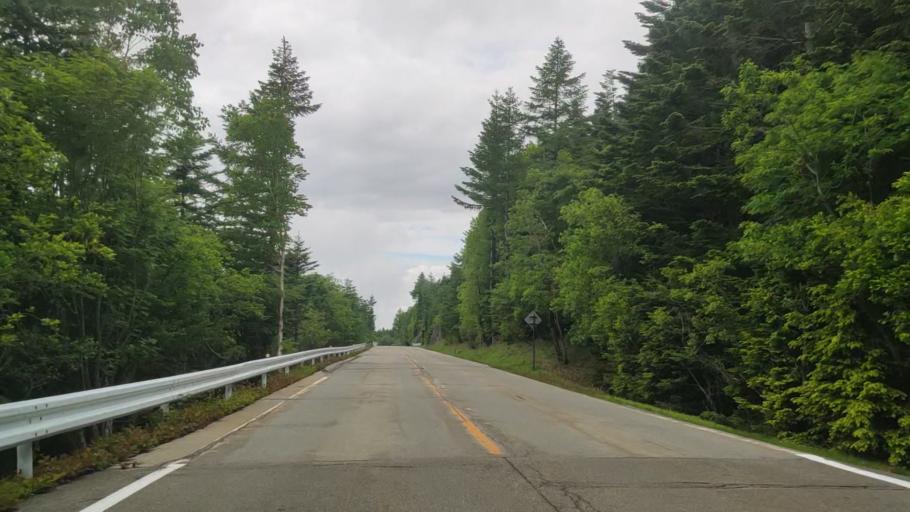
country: JP
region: Yamanashi
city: Fujikawaguchiko
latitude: 35.3835
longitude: 138.6909
